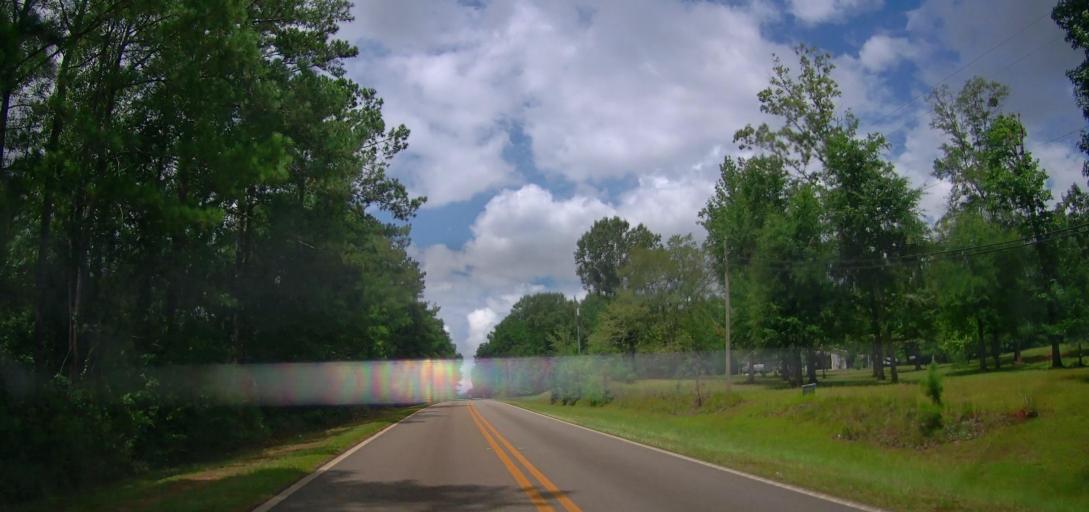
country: US
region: Georgia
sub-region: Pulaski County
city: Hawkinsville
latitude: 32.3356
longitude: -83.5392
